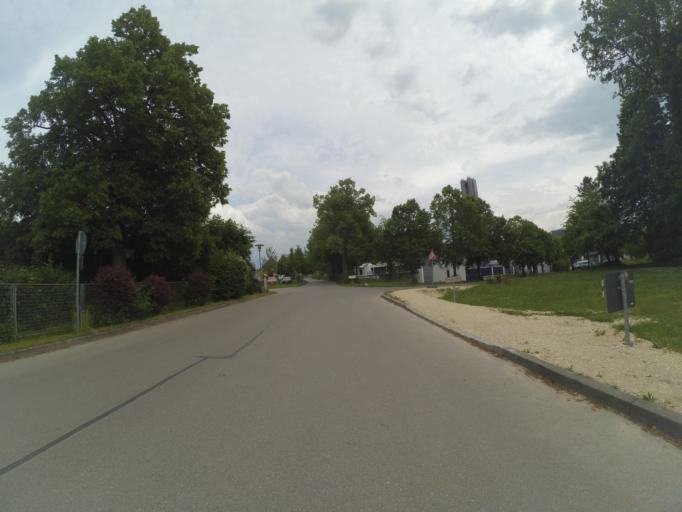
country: DE
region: Bavaria
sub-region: Swabia
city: Guenzburg
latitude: 48.4605
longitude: 10.2933
